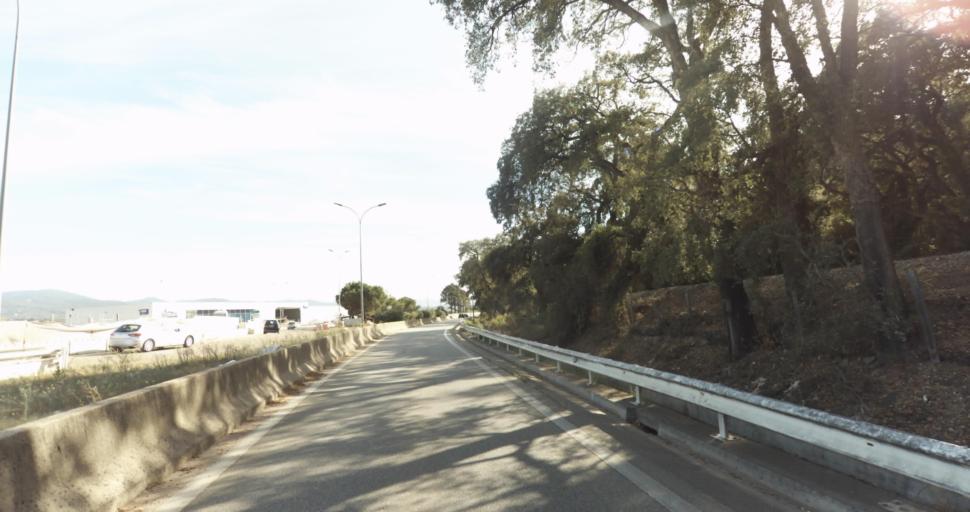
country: FR
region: Corsica
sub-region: Departement de la Corse-du-Sud
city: Afa
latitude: 41.9317
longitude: 8.8018
